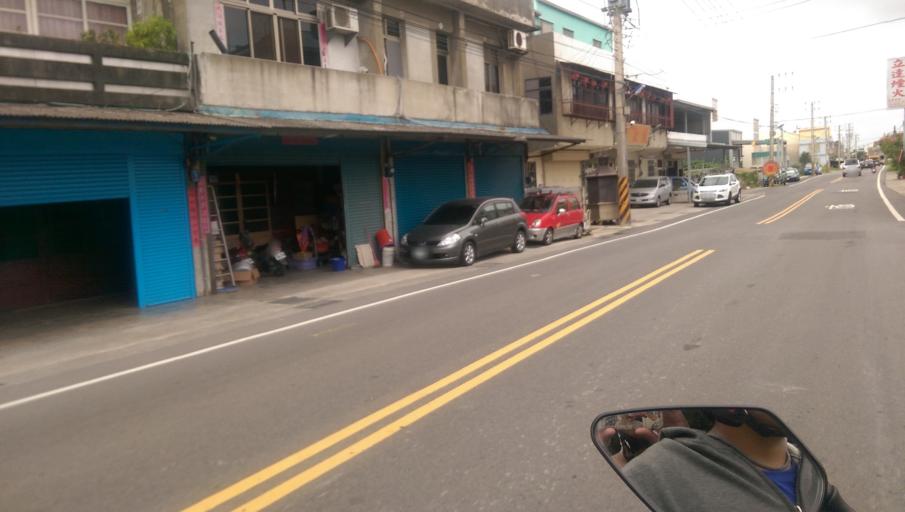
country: TW
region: Taiwan
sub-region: Hsinchu
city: Hsinchu
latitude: 24.8153
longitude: 120.9289
